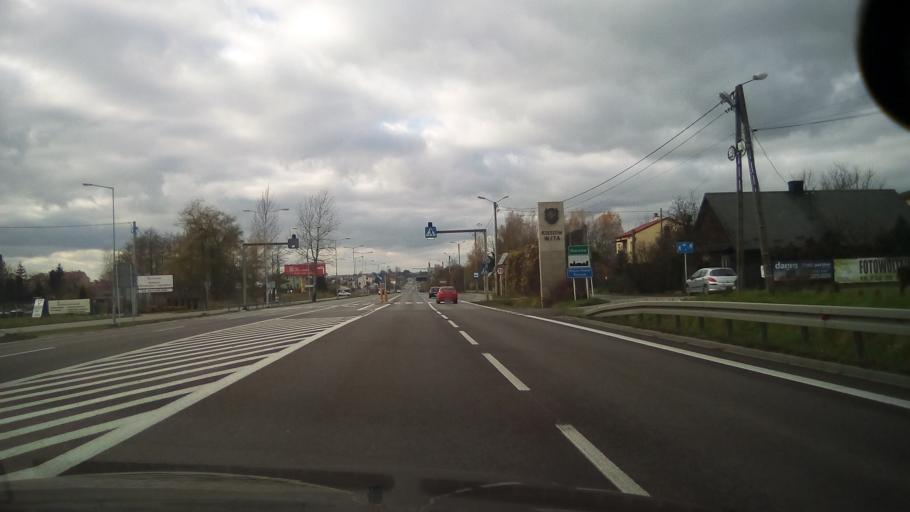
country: PL
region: Subcarpathian Voivodeship
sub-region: Powiat rzeszowski
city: Krasne
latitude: 50.0395
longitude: 22.0639
